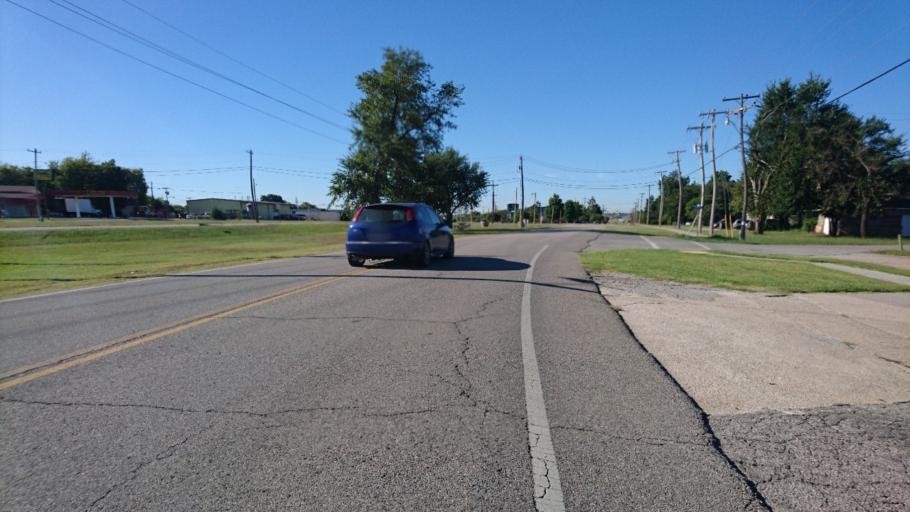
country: US
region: Oklahoma
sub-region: Rogers County
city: Catoosa
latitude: 36.1805
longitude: -95.7493
